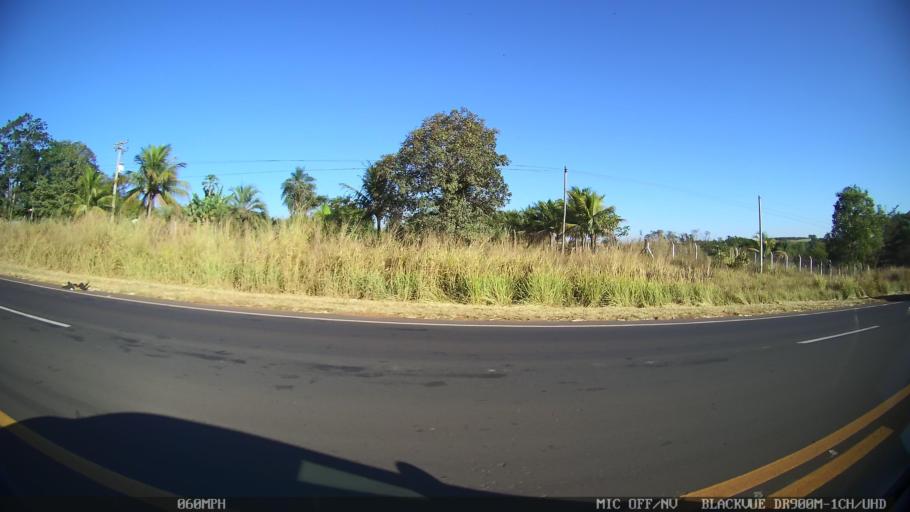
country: BR
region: Sao Paulo
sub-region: Olimpia
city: Olimpia
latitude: -20.7059
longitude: -48.9565
